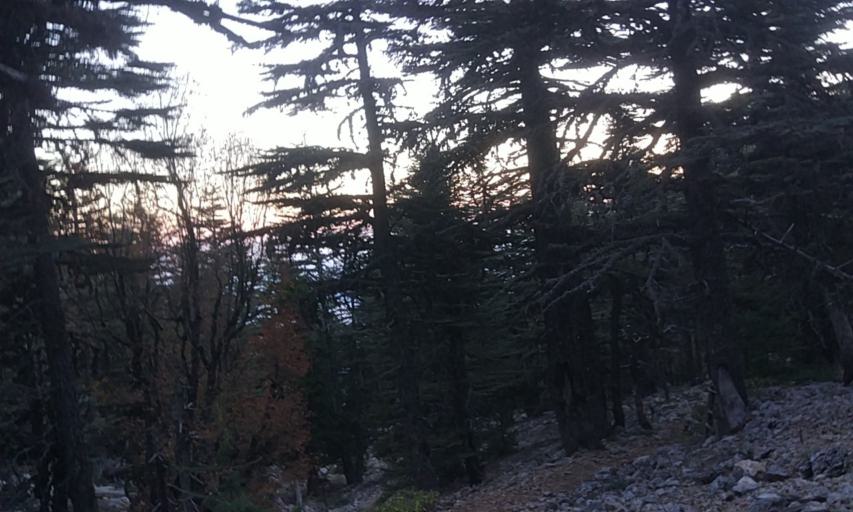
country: TR
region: Antalya
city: Altinyaka
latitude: 36.5367
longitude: 30.4173
